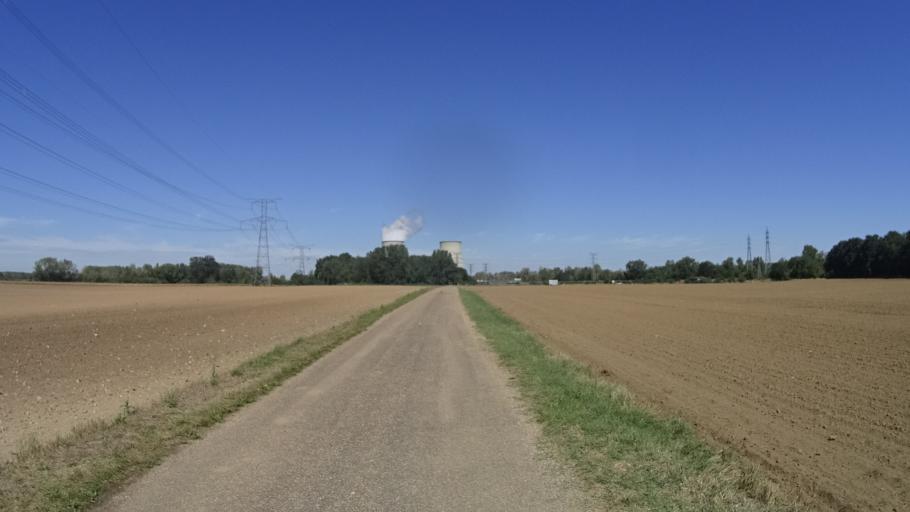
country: FR
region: Bourgogne
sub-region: Departement de la Nievre
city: Neuvy-sur-Loire
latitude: 47.4957
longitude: 2.8881
